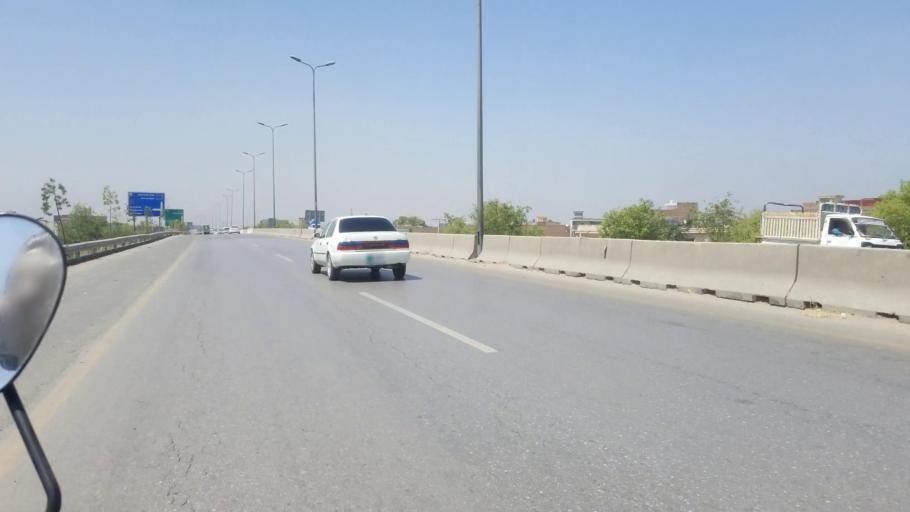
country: PK
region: Khyber Pakhtunkhwa
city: Peshawar
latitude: 34.0250
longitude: 71.6304
